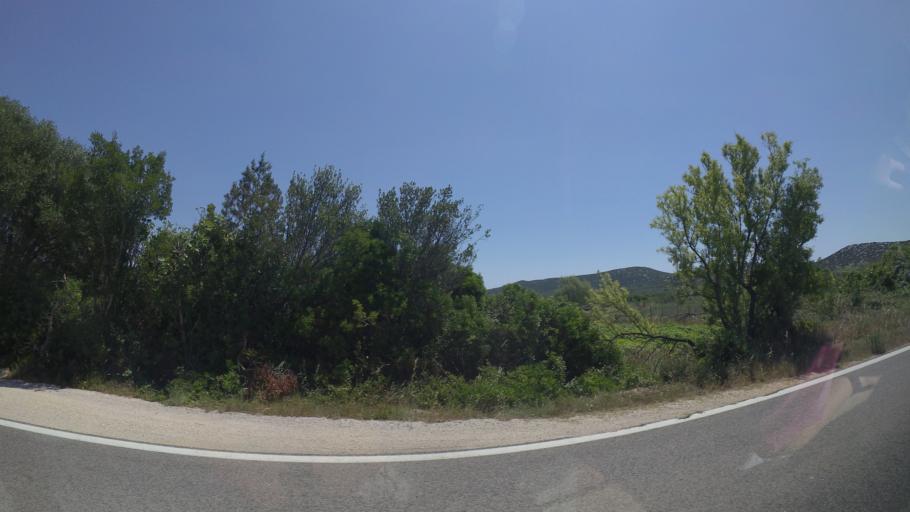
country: HR
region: Sibensko-Kniniska
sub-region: Grad Sibenik
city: Pirovac
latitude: 43.8007
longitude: 15.6907
